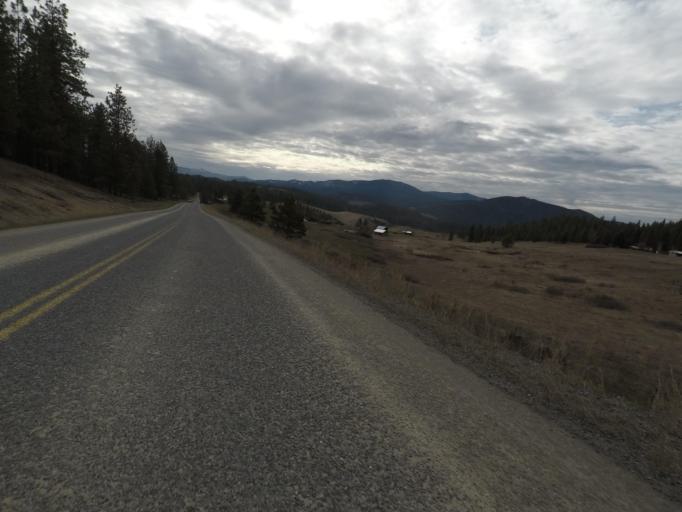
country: US
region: Washington
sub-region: Stevens County
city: Colville
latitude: 48.5013
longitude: -117.8486
